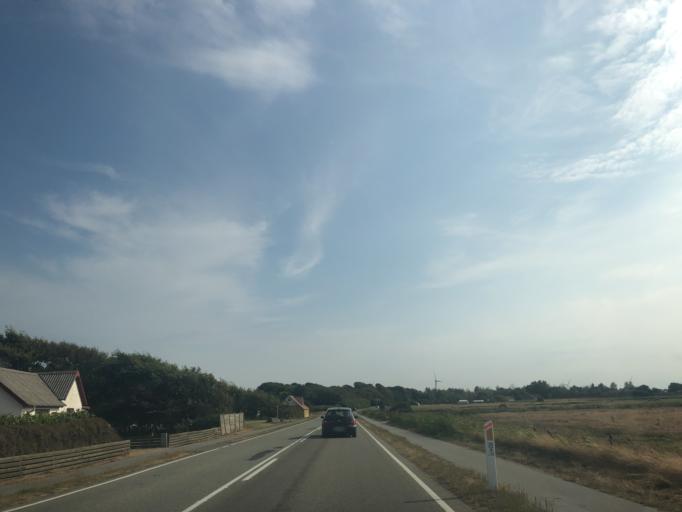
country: DK
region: North Denmark
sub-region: Morso Kommune
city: Nykobing Mors
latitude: 56.7879
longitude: 9.0437
